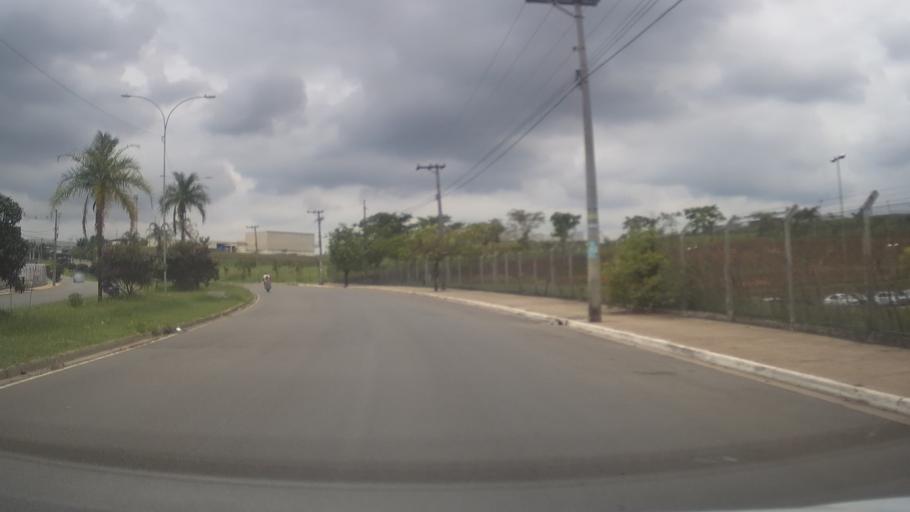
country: BR
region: Sao Paulo
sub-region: Itupeva
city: Itupeva
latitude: -23.1503
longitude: -47.0170
